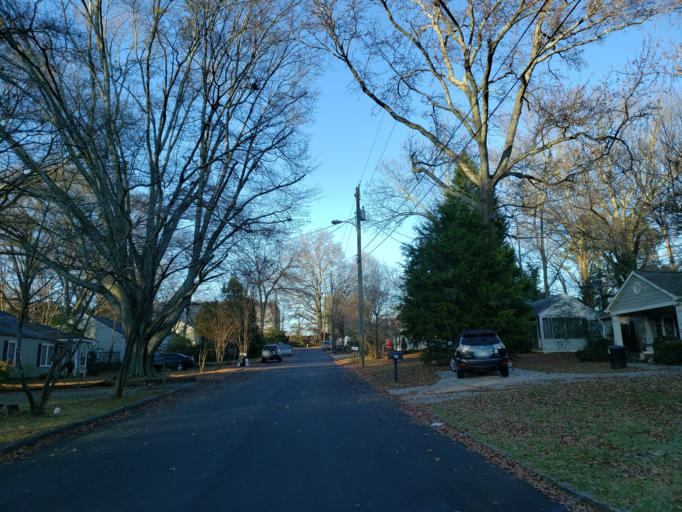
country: US
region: Georgia
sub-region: Cobb County
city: Marietta
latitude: 33.9488
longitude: -84.5385
